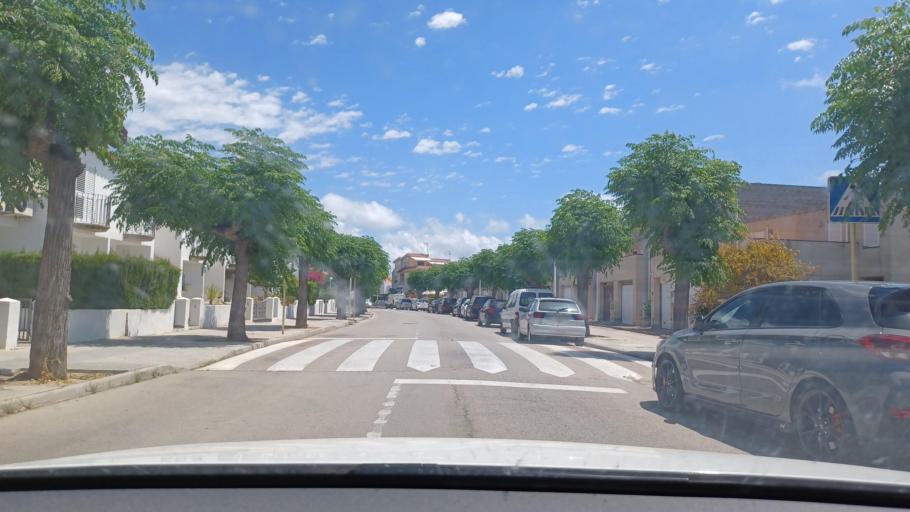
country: ES
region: Catalonia
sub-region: Provincia de Tarragona
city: Sant Carles de la Rapita
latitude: 40.6116
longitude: 0.5860
